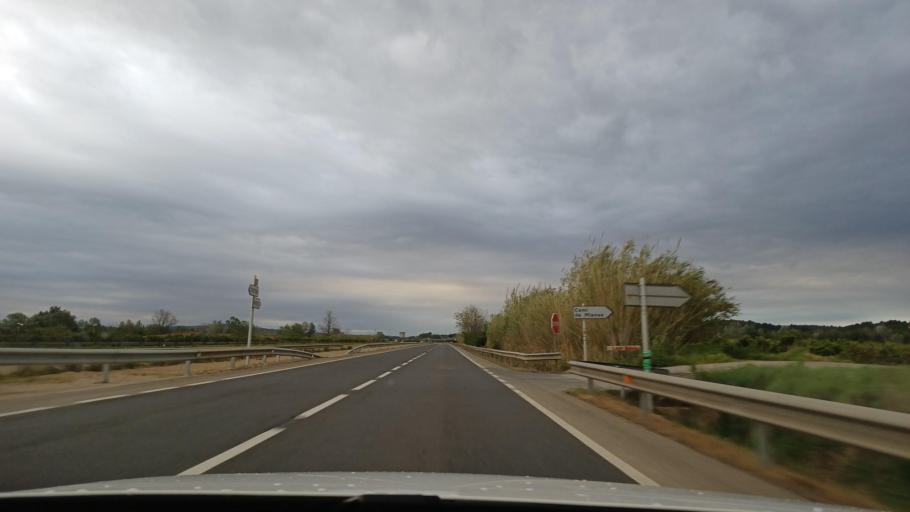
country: ES
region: Catalonia
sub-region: Provincia de Tarragona
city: Masdenverge
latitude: 40.7546
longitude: 0.5405
